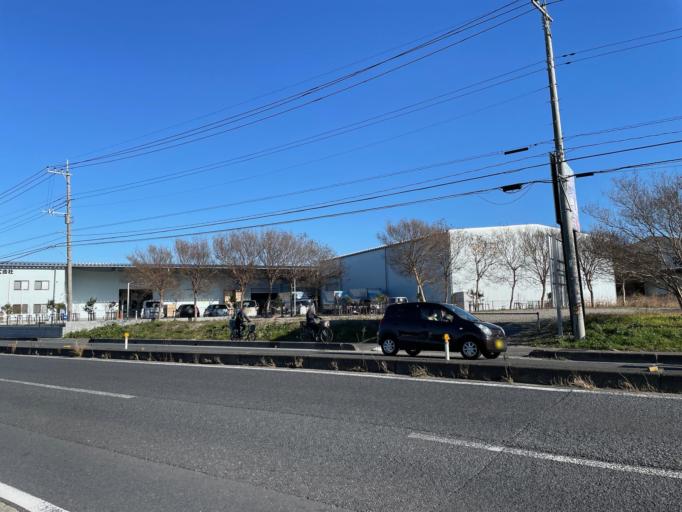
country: JP
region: Saitama
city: Hasuda
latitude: 35.9694
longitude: 139.6342
